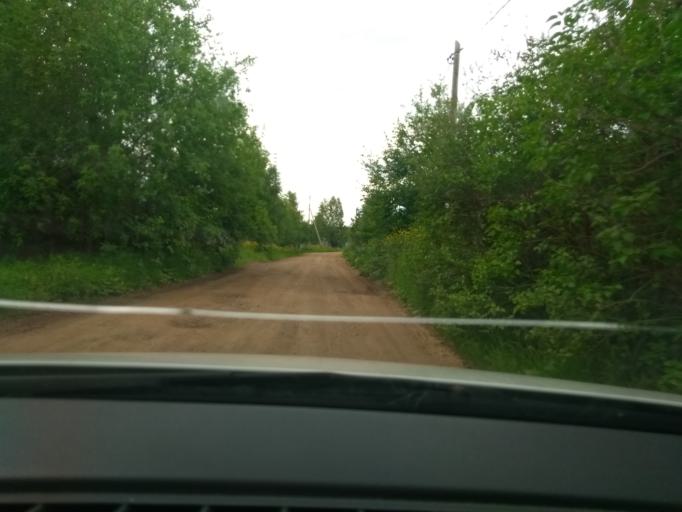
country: RU
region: Perm
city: Sylva
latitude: 57.8434
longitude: 56.7958
